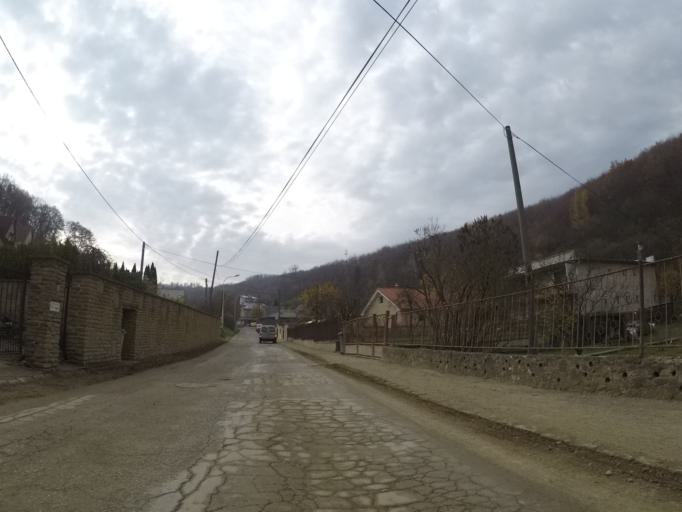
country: SK
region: Presovsky
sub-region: Okres Presov
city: Presov
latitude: 48.9837
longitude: 21.2180
